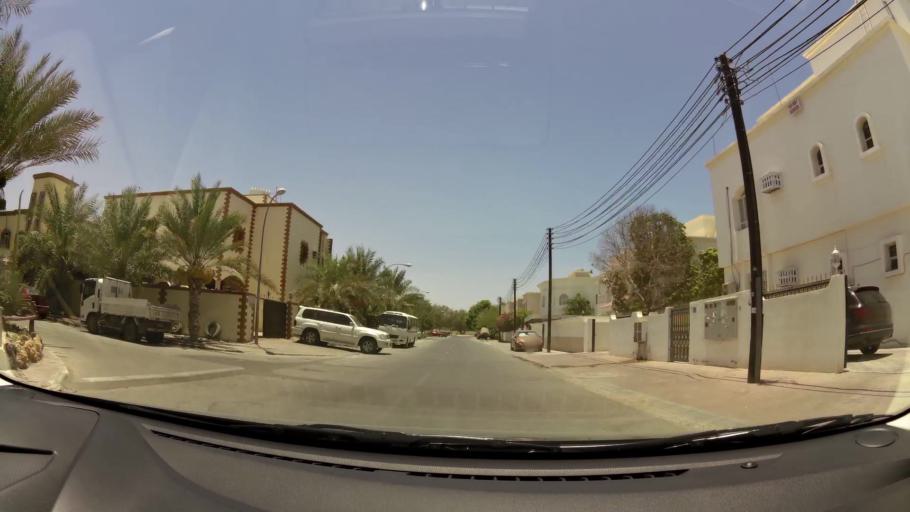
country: OM
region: Muhafazat Masqat
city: Bawshar
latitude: 23.5952
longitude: 58.3918
